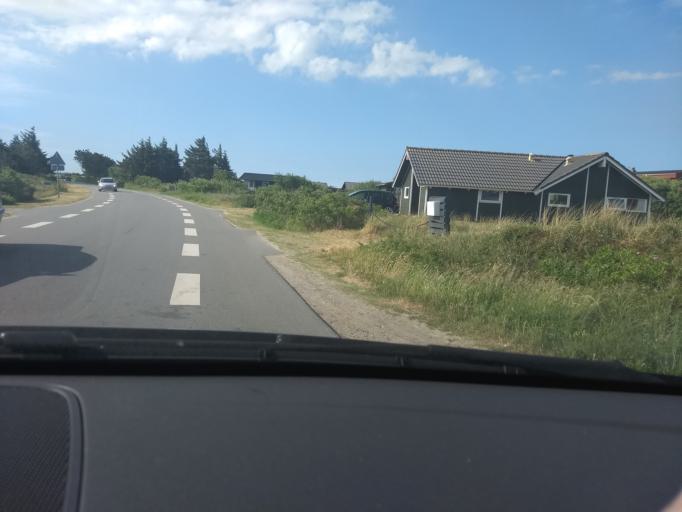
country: DE
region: Schleswig-Holstein
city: List
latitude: 55.1438
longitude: 8.4942
